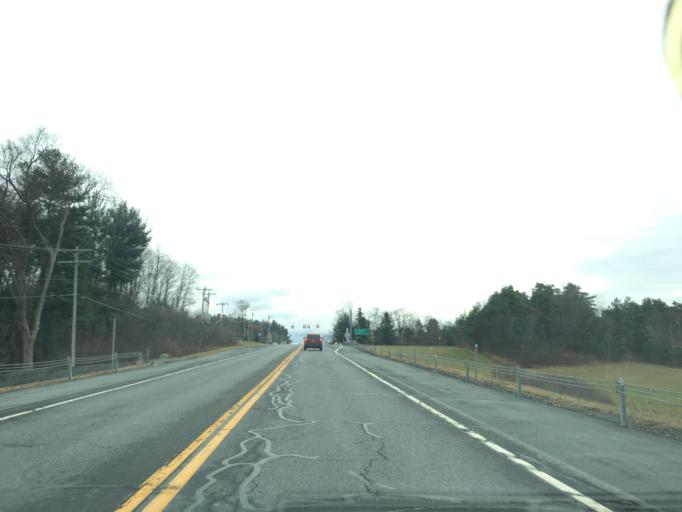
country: US
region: New York
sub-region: Rensselaer County
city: Poestenkill
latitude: 42.6653
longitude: -73.5816
